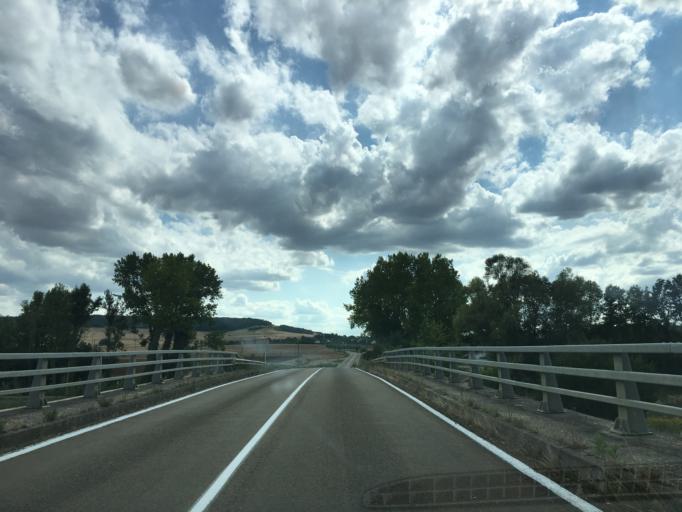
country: FR
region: Bourgogne
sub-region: Departement de l'Yonne
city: Joigny
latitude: 47.9657
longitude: 3.3848
